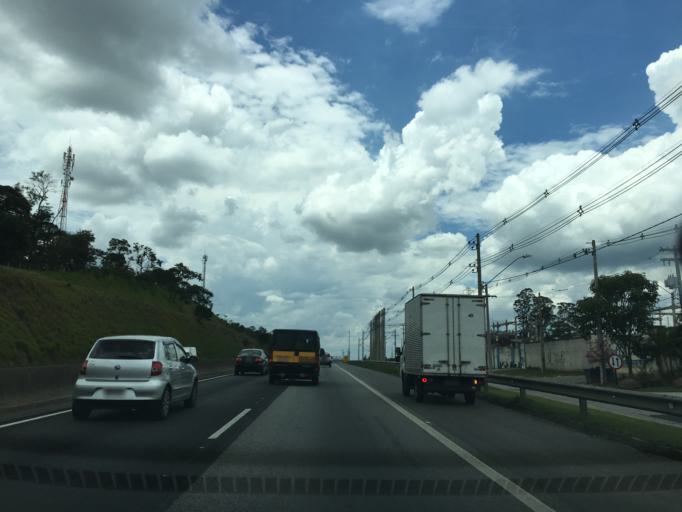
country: BR
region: Sao Paulo
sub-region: Atibaia
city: Atibaia
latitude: -23.2087
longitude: -46.5919
